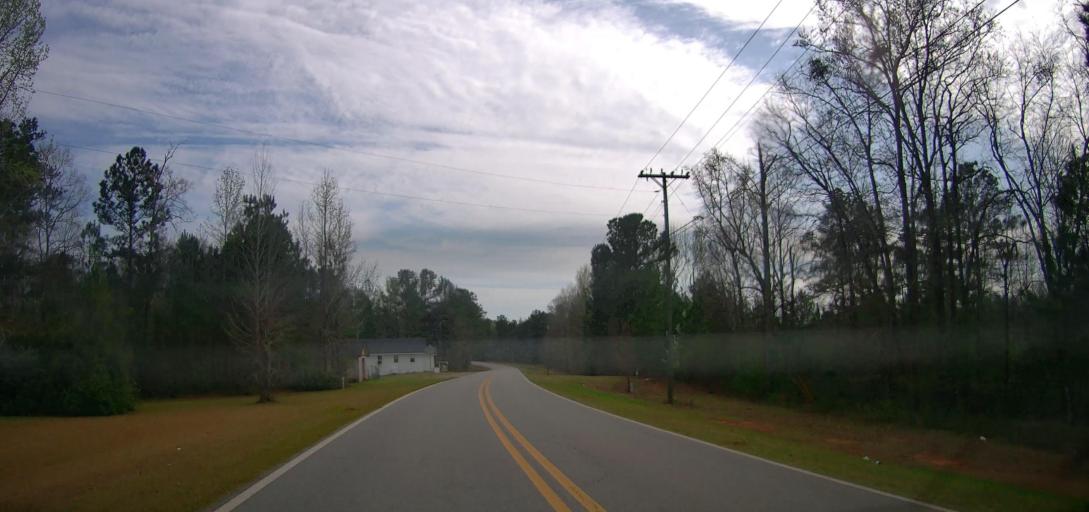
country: US
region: Georgia
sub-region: Bibb County
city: Macon
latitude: 32.9545
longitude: -83.6527
